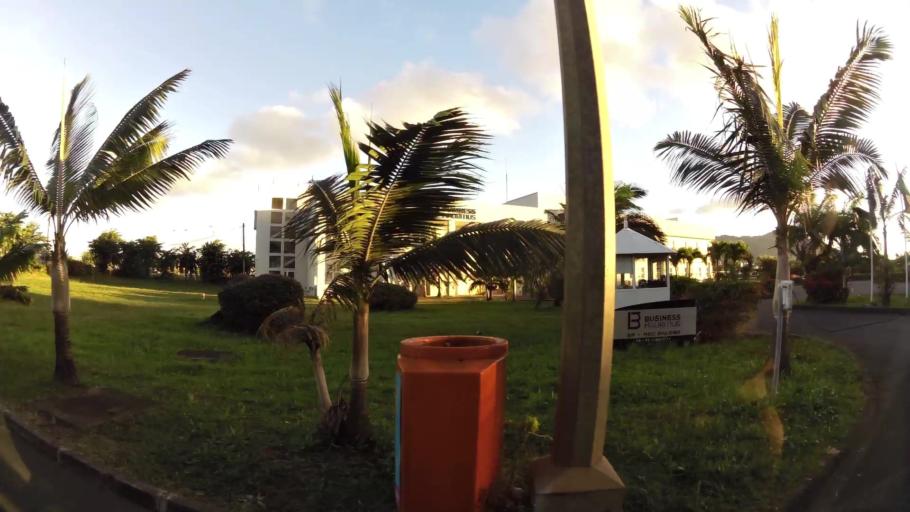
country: MU
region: Plaines Wilhems
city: Ebene
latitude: -20.2460
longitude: 57.4895
